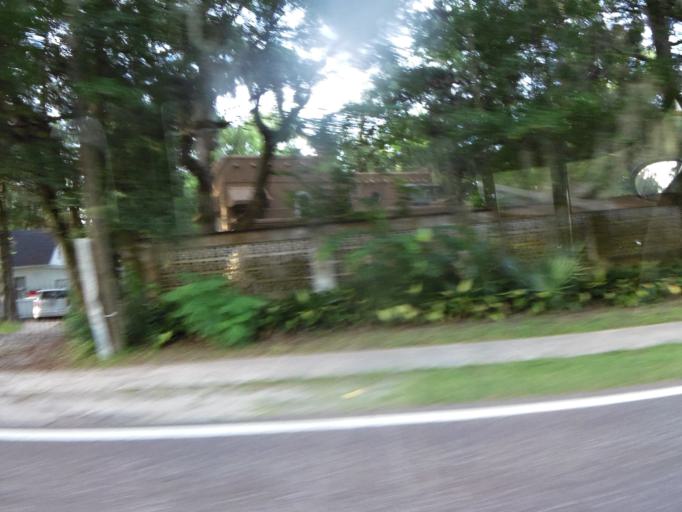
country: US
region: Florida
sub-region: Duval County
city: Jacksonville
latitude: 30.4154
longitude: -81.7024
